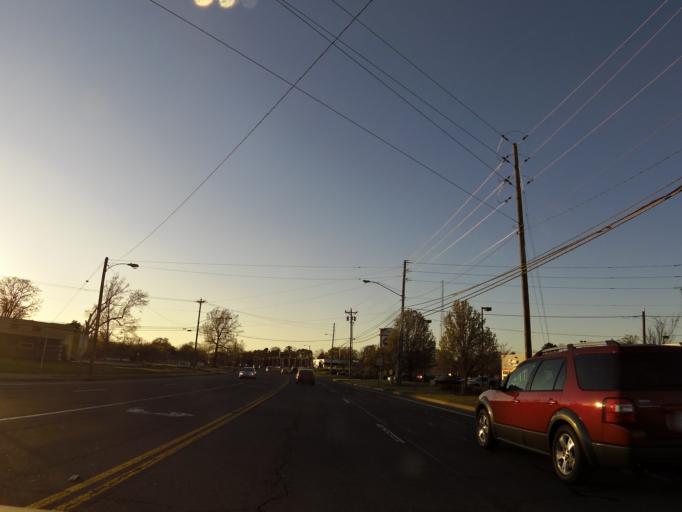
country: US
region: Tennessee
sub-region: Robertson County
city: Springfield
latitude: 36.4866
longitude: -86.8641
